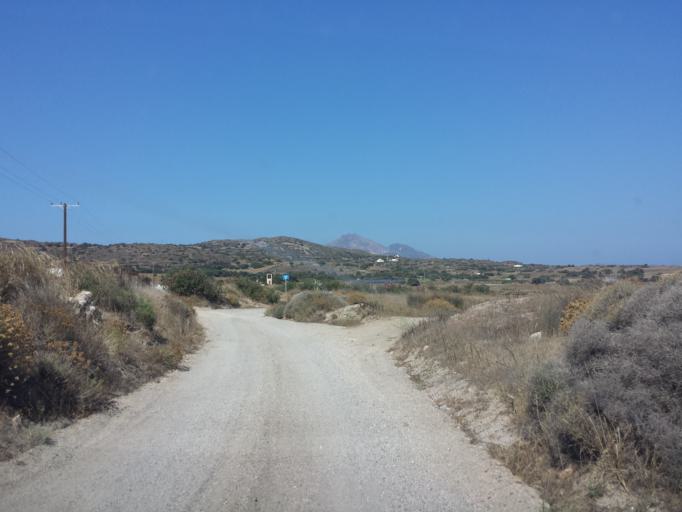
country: GR
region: South Aegean
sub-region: Nomos Kykladon
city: Adamas
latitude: 36.6871
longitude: 24.4901
